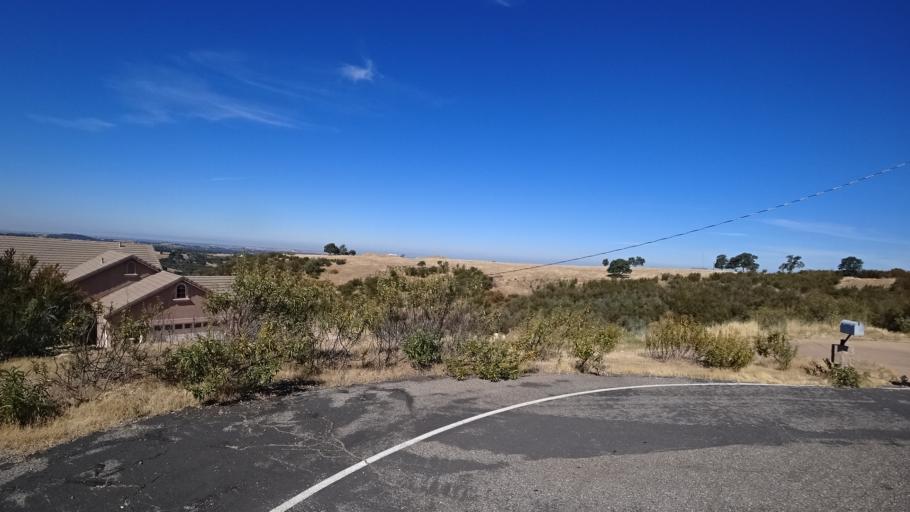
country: US
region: California
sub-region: Calaveras County
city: Rancho Calaveras
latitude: 38.1698
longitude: -120.8666
